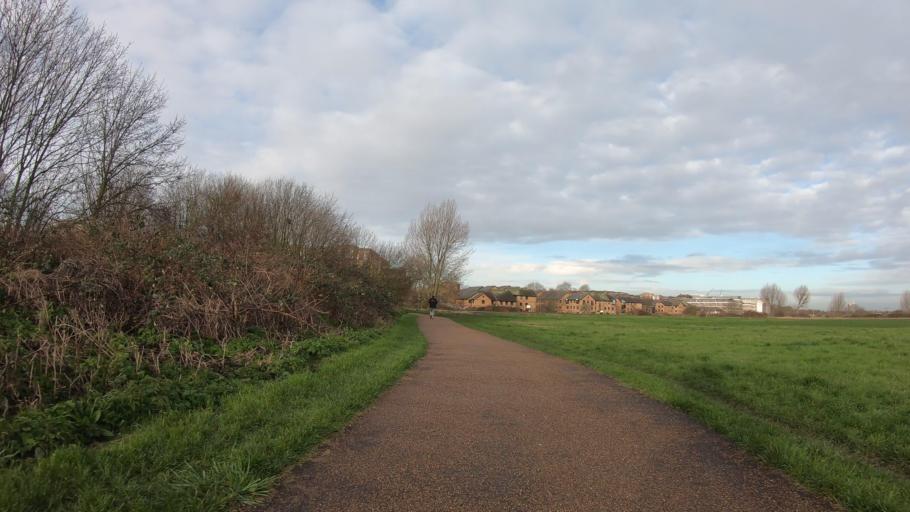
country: GB
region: England
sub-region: Greater London
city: Hackney
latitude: 51.5605
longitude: -0.0332
